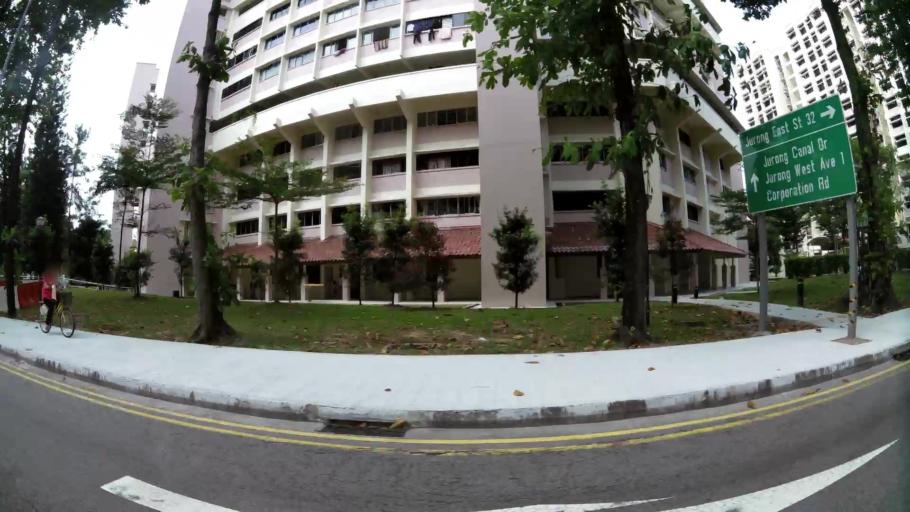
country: MY
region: Johor
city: Johor Bahru
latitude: 1.3471
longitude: 103.7315
